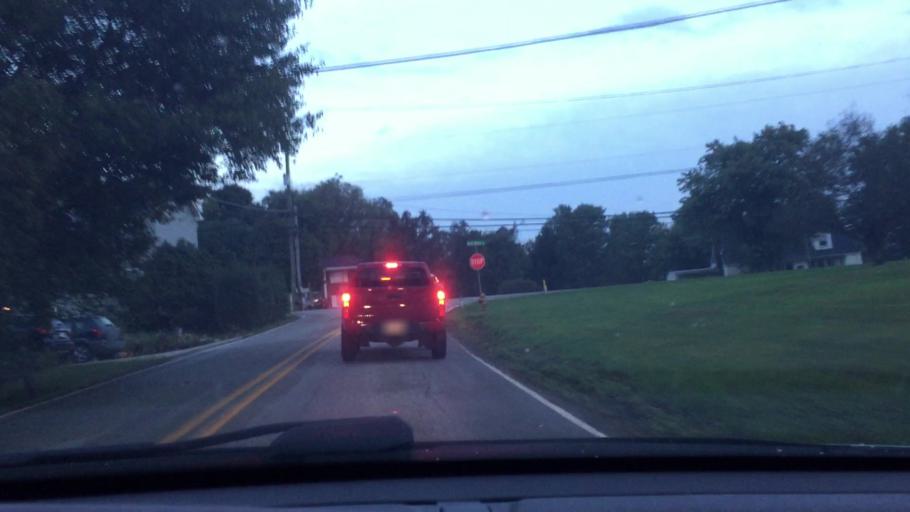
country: US
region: Pennsylvania
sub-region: Washington County
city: East Washington
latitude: 40.1828
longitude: -80.1812
